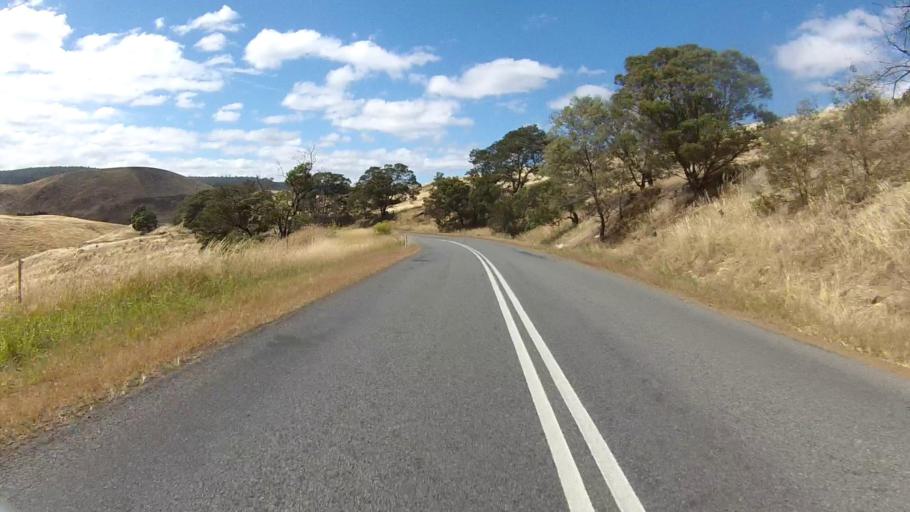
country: AU
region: Tasmania
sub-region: Brighton
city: Bridgewater
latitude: -42.5709
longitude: 147.3948
